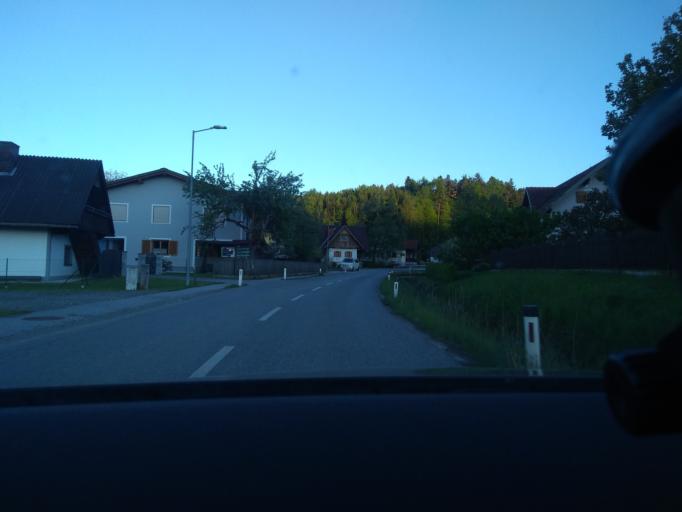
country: AT
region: Styria
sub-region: Politischer Bezirk Voitsberg
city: Mooskirchen
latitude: 46.9752
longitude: 15.2839
